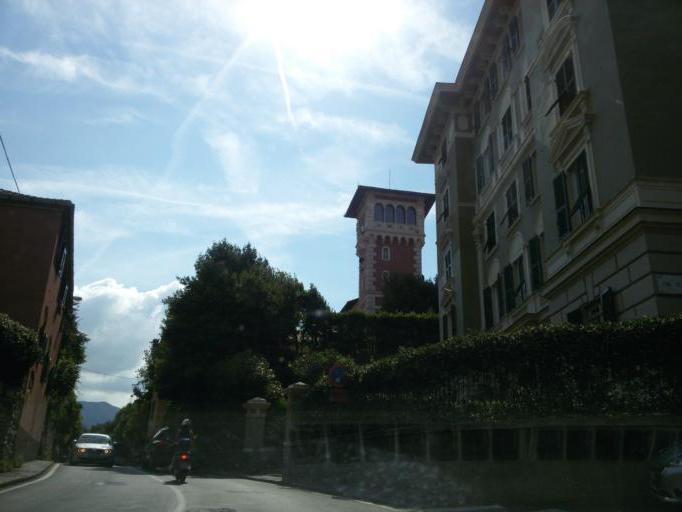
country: IT
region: Liguria
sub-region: Provincia di Genova
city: Genoa
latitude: 44.3961
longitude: 8.9704
